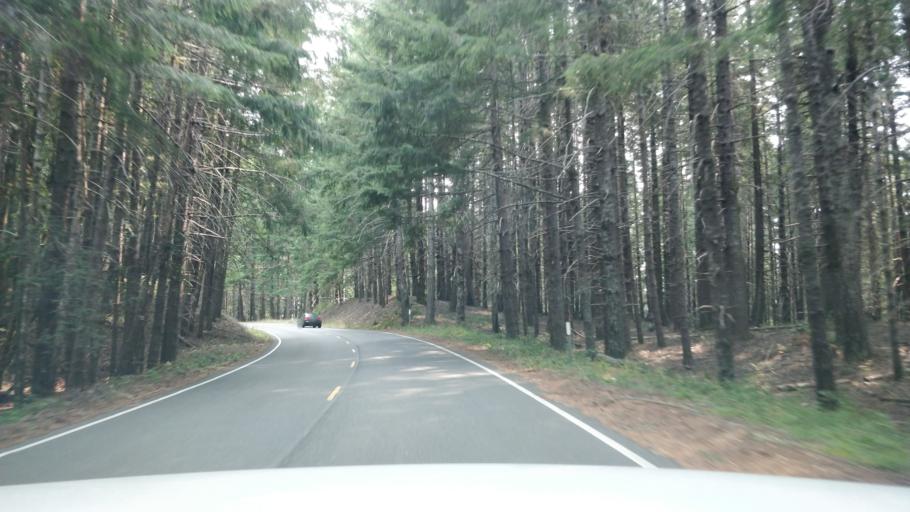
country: US
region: California
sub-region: Humboldt County
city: Westhaven-Moonstone
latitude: 41.2101
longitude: -123.9565
